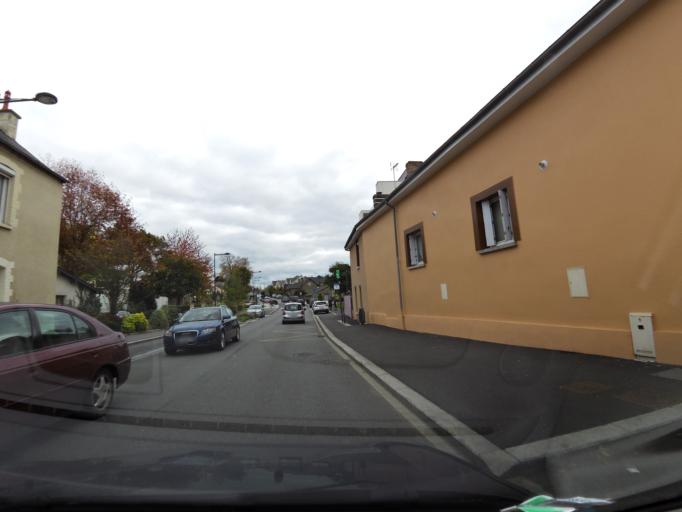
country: FR
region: Brittany
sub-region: Departement d'Ille-et-Vilaine
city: Chantepie
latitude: 48.0878
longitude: -1.6171
